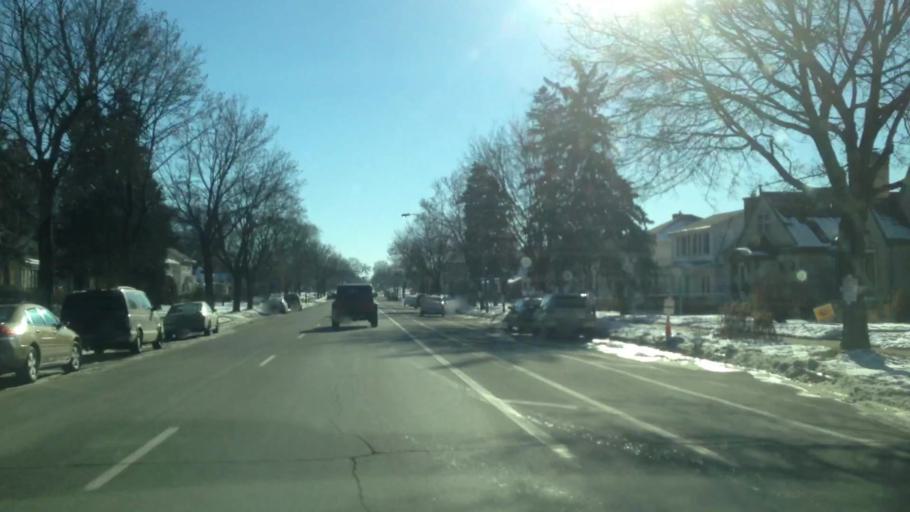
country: US
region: Minnesota
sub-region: Hennepin County
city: Minneapolis
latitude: 44.9305
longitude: -93.2676
